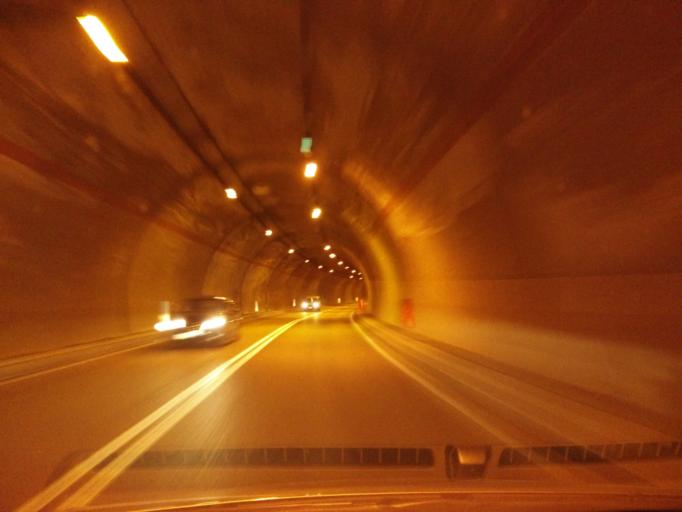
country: IT
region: Veneto
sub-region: Provincia di Belluno
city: Pieve di Cadore
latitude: 46.4297
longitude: 12.3790
